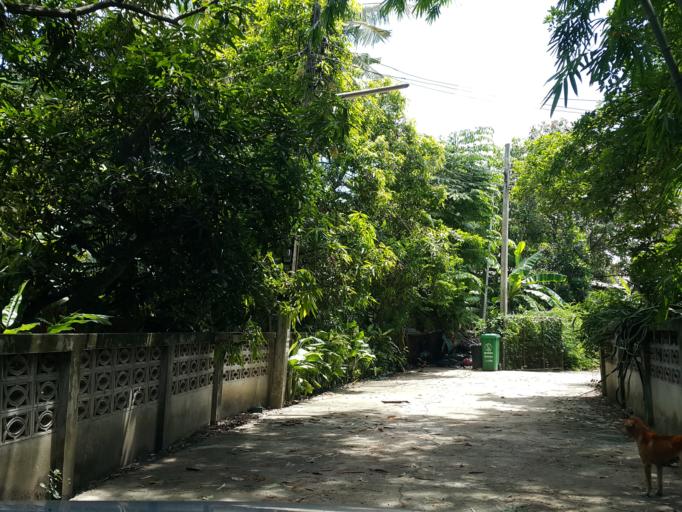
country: TH
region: Chiang Mai
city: San Kamphaeng
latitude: 18.7603
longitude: 99.0961
